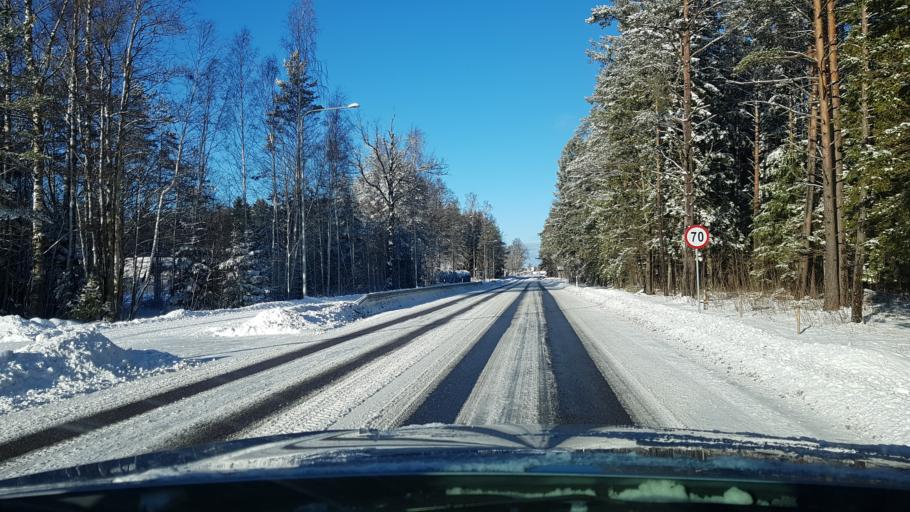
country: EE
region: Hiiumaa
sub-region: Kaerdla linn
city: Kardla
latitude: 58.9804
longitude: 22.7592
